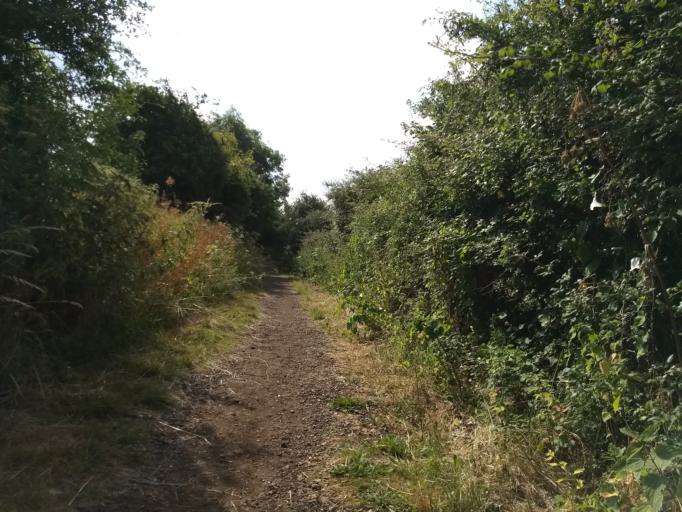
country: GB
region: England
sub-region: Isle of Wight
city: Ryde
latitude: 50.7149
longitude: -1.1585
